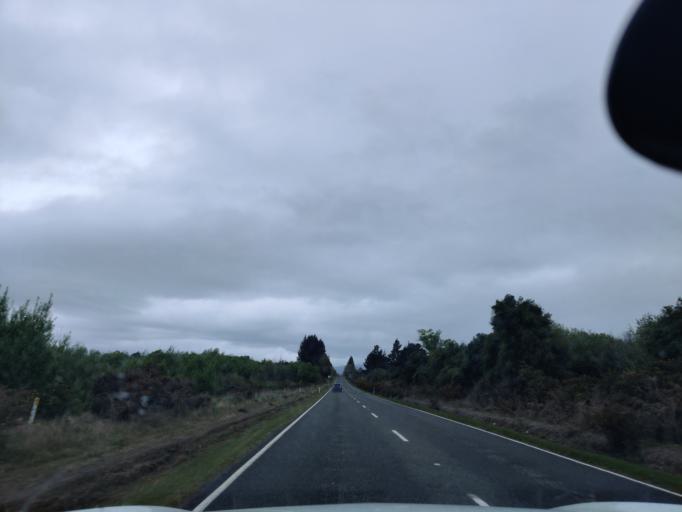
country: NZ
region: Waikato
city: Turangi
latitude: -38.9869
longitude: 175.7877
